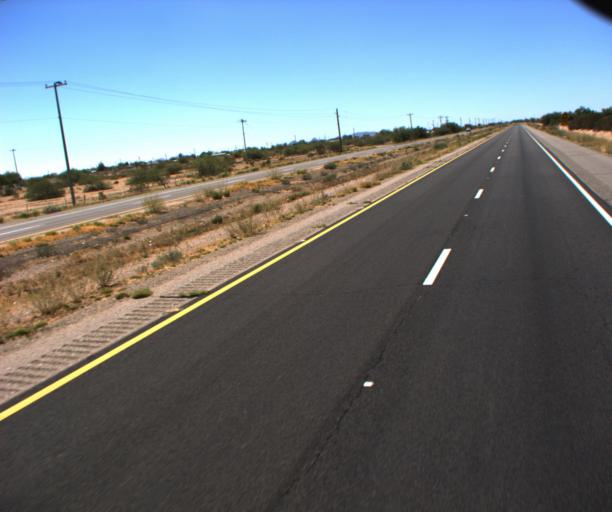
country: US
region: Arizona
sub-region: Pinal County
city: Maricopa
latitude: 32.8904
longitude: -112.0496
